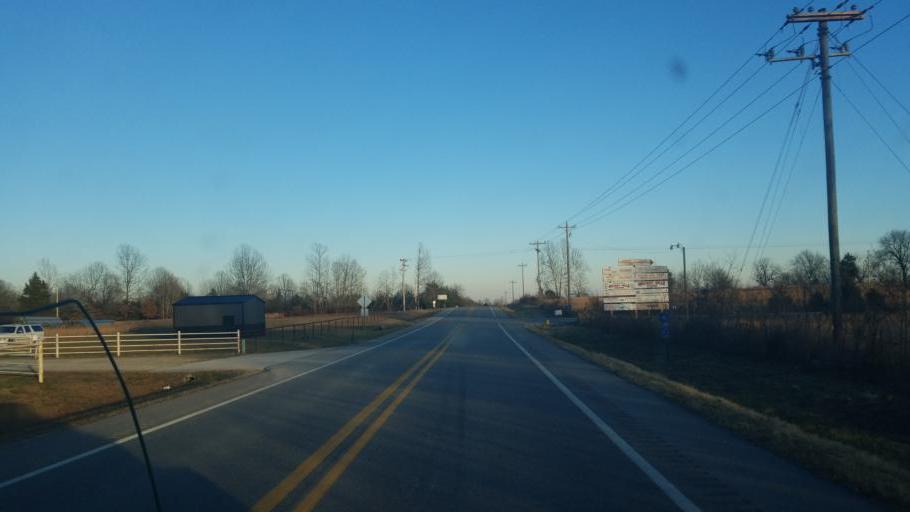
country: US
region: Arkansas
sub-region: Baxter County
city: Mountain Home
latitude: 36.3757
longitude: -92.1472
